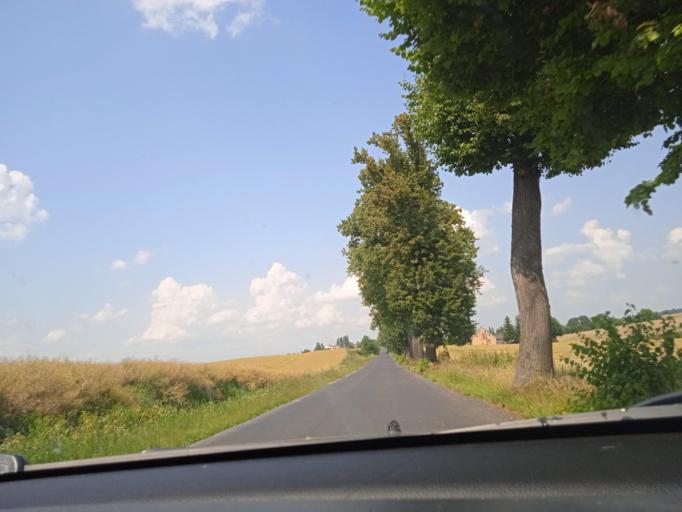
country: PL
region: Kujawsko-Pomorskie
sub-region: Powiat grudziadzki
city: Lasin
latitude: 53.5403
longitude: 19.0678
